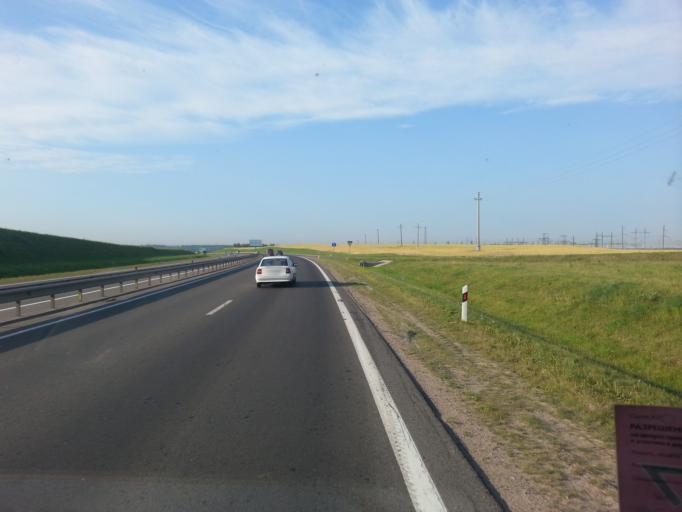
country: BY
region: Minsk
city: Bal'shavik
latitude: 54.0036
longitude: 27.5366
